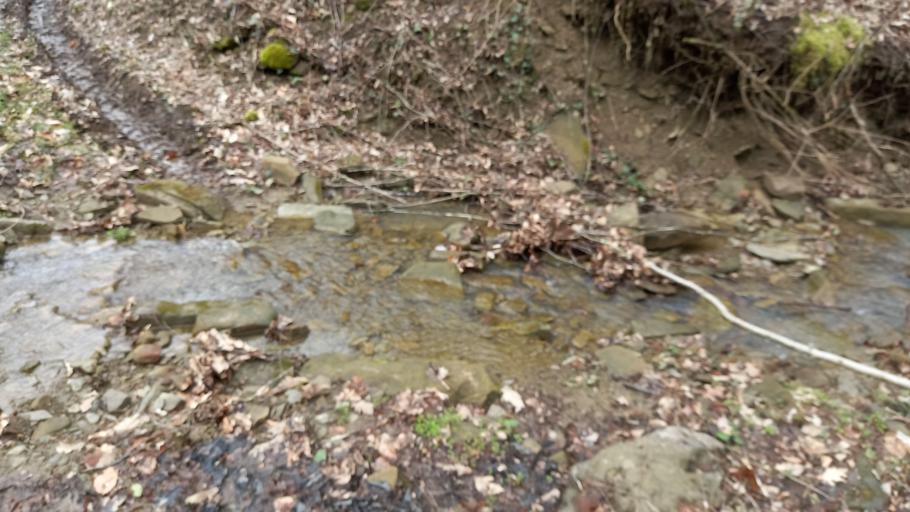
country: RU
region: Krasnodarskiy
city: Pshada
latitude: 44.4915
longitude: 38.3901
